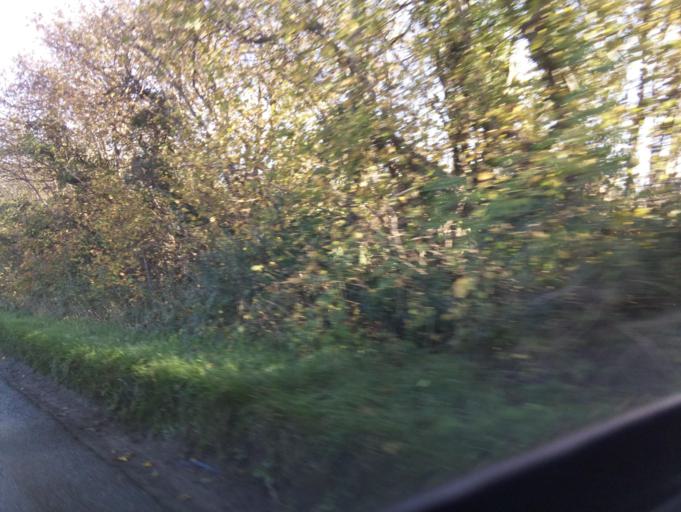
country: GB
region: England
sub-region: Somerset
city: Frome
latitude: 51.1937
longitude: -2.3869
